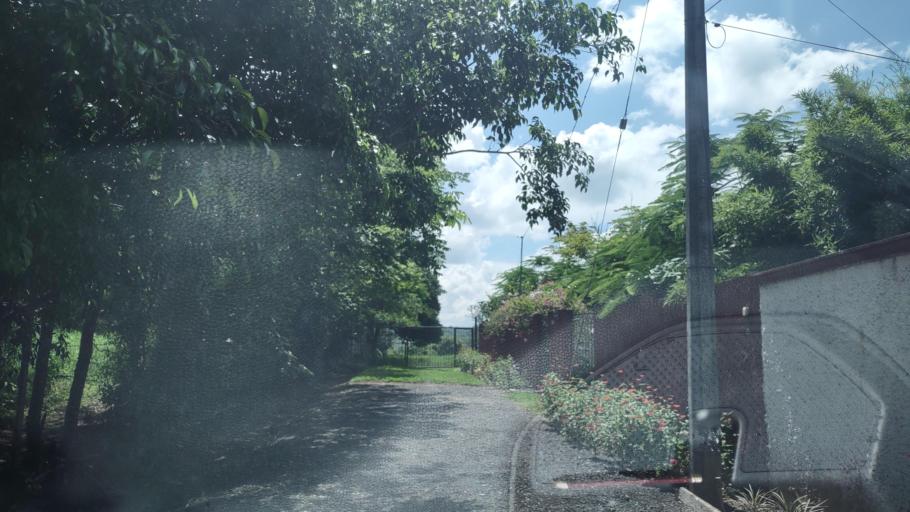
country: MX
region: Veracruz
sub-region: Emiliano Zapata
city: Dos Rios
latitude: 19.4953
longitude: -96.8075
